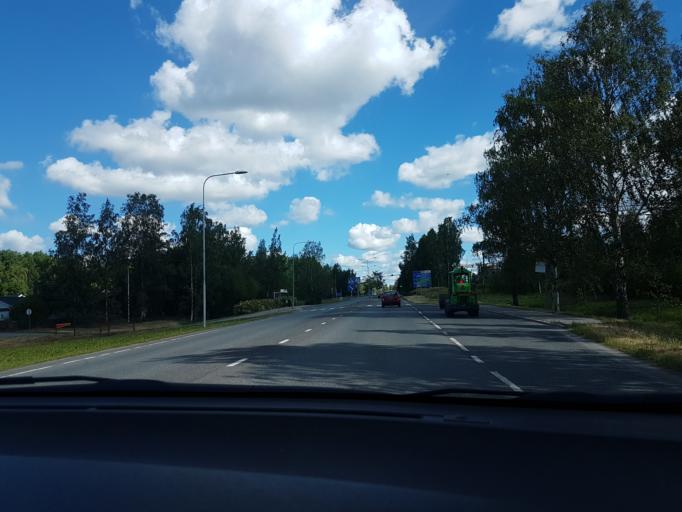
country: FI
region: Uusimaa
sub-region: Helsinki
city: Kerava
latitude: 60.3923
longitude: 25.1012
